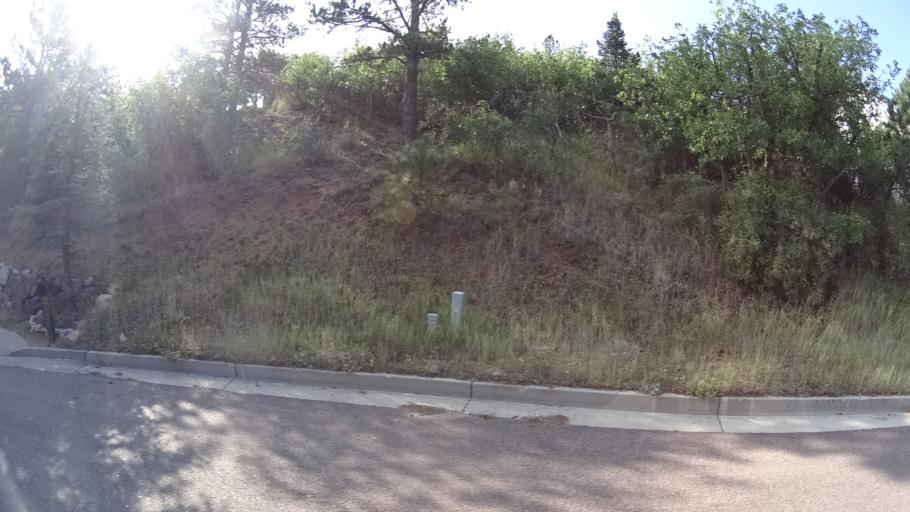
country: US
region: Colorado
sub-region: El Paso County
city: Colorado Springs
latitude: 38.8239
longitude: -104.8715
